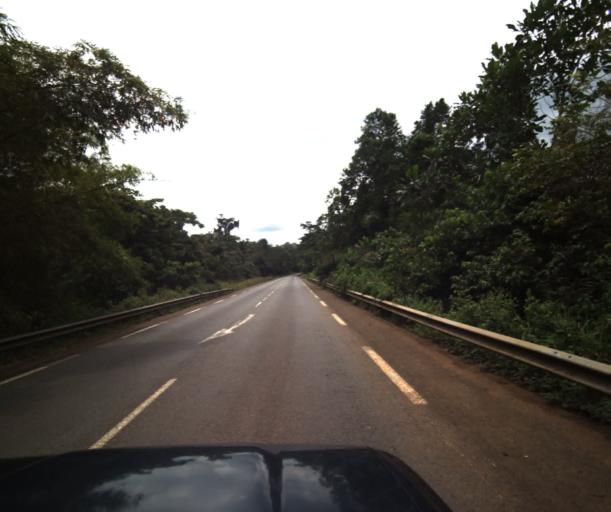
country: CM
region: Centre
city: Eseka
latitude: 3.8813
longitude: 10.6947
